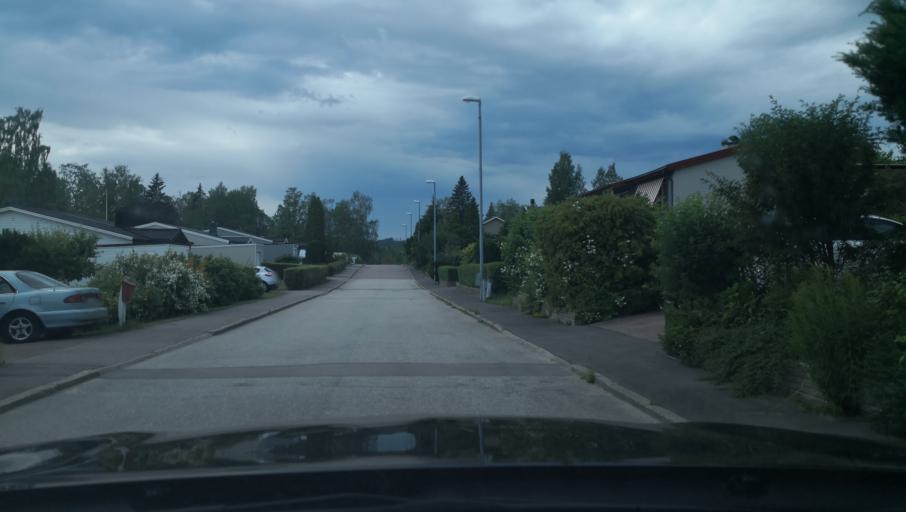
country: SE
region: Vaestmanland
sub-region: Fagersta Kommun
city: Fagersta
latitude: 59.9838
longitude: 15.8300
